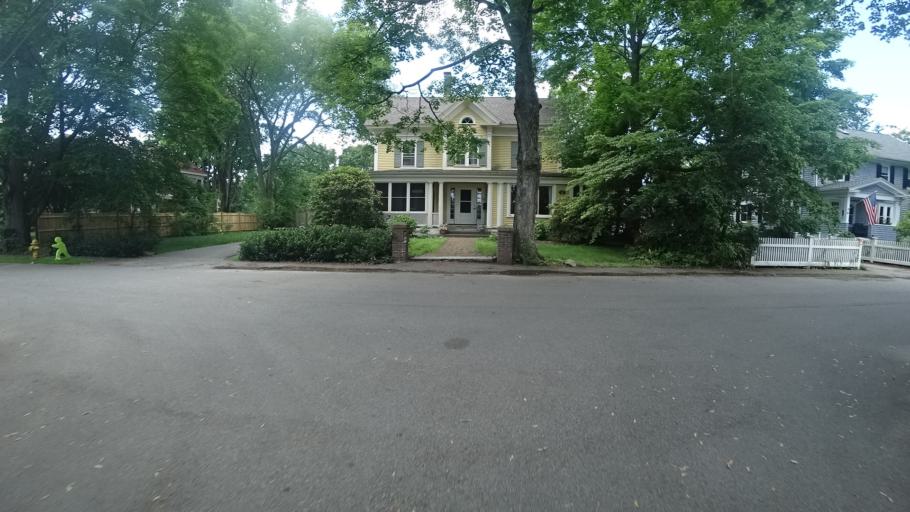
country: US
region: Massachusetts
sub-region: Norfolk County
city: Dedham
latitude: 42.2445
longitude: -71.1748
